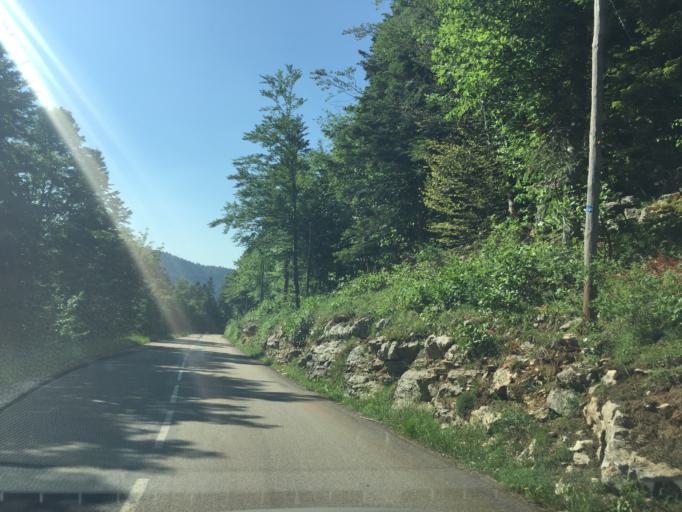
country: FR
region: Rhone-Alpes
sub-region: Departement de la Drome
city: Saint-Jean-en-Royans
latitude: 44.9269
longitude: 5.3249
